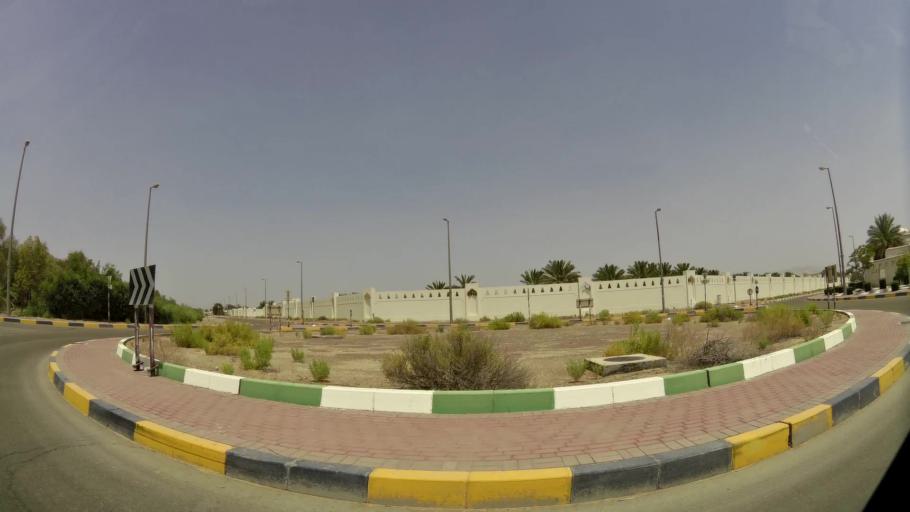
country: AE
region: Abu Dhabi
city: Al Ain
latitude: 24.1918
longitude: 55.6781
